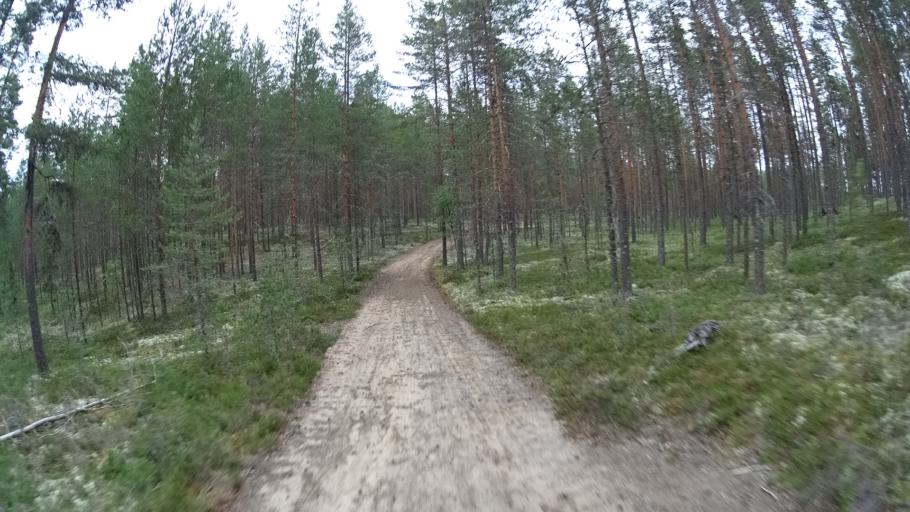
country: FI
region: Satakunta
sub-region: Pohjois-Satakunta
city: Jaemijaervi
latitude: 61.7620
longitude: 22.7565
